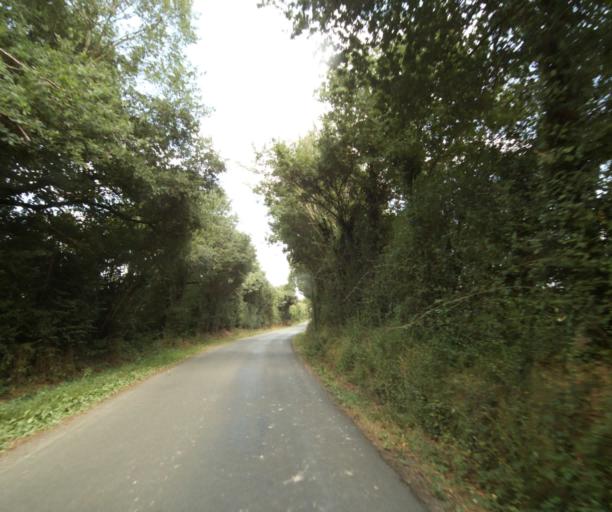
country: FR
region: Pays de la Loire
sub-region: Departement de la Sarthe
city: Auvers-le-Hamon
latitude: 47.8667
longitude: -0.3600
